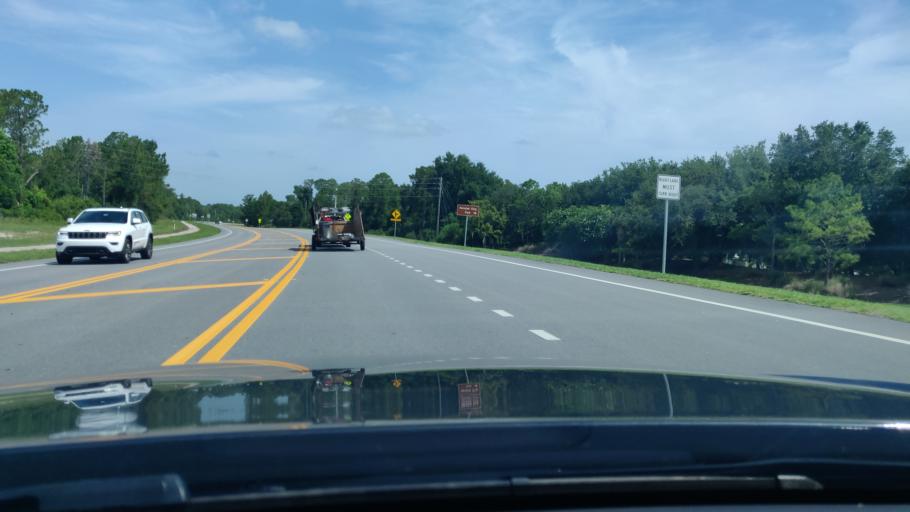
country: US
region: Florida
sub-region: Flagler County
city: Flagler Beach
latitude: 29.5178
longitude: -81.1652
